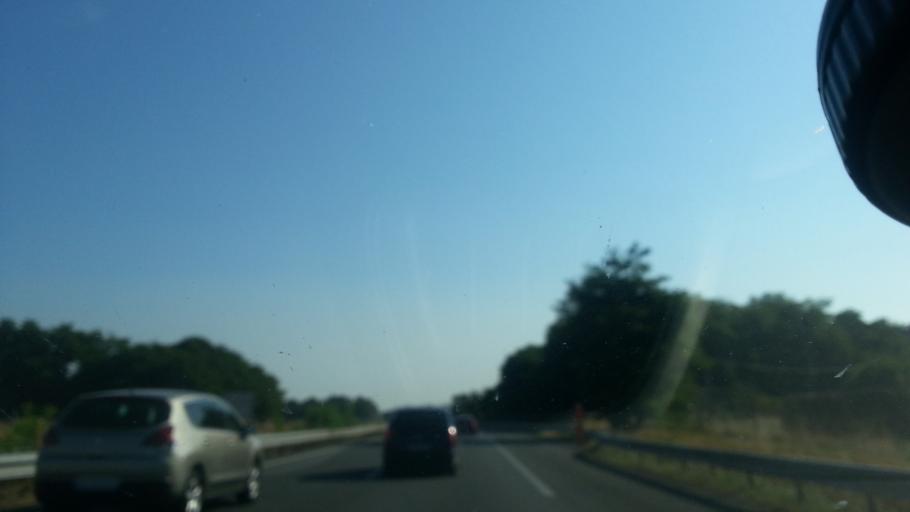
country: FR
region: Poitou-Charentes
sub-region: Departement de la Vienne
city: Naintre
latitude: 46.7760
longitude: 0.4934
